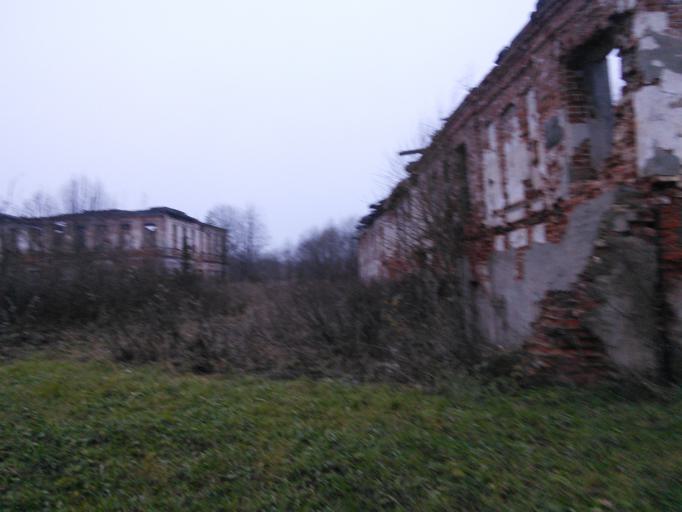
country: RU
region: Vologda
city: Kharovsk
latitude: 59.7792
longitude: 40.1956
